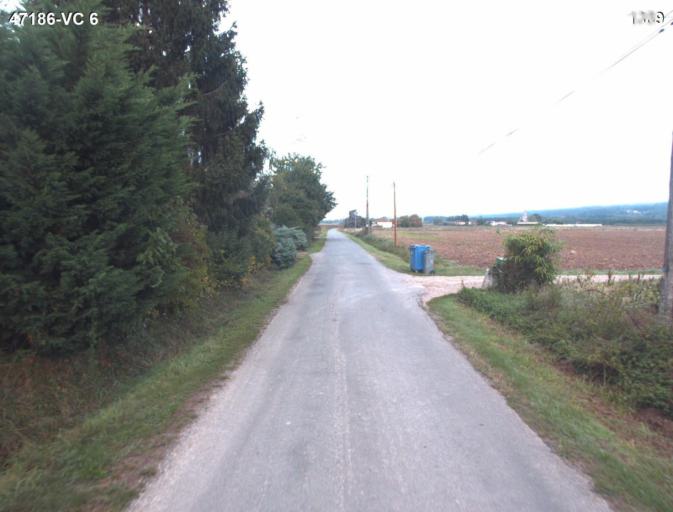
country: FR
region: Aquitaine
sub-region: Departement du Lot-et-Garonne
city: Port-Sainte-Marie
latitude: 44.2230
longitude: 0.4530
